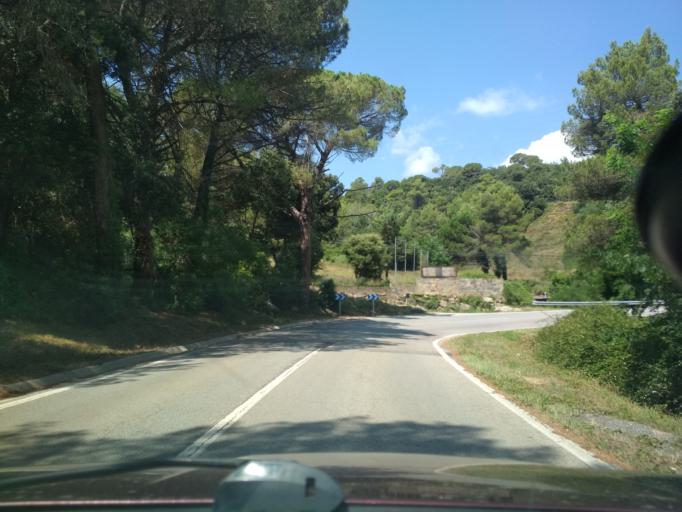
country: ES
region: Catalonia
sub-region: Provincia de Barcelona
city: Sant Feliu de Codines
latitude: 41.7066
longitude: 2.1560
